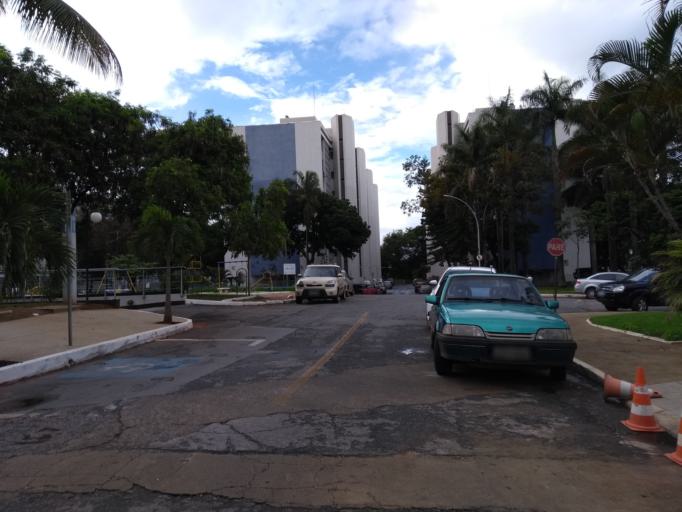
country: BR
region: Federal District
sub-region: Brasilia
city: Brasilia
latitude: -15.7432
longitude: -47.8965
